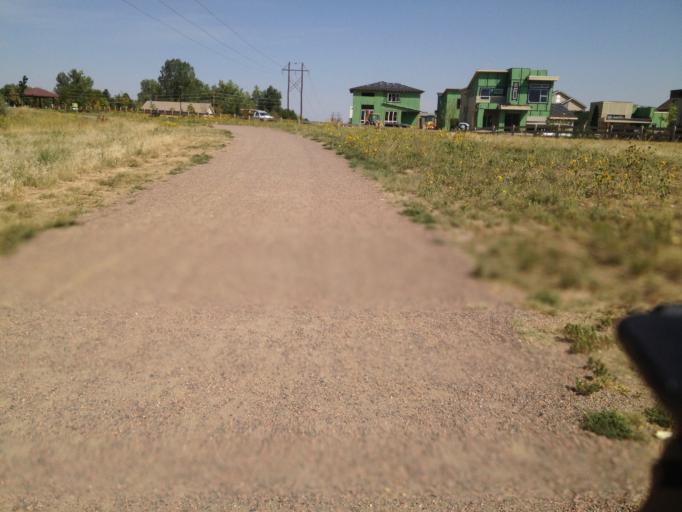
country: US
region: Colorado
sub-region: Boulder County
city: Louisville
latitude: 39.9904
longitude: -105.1209
